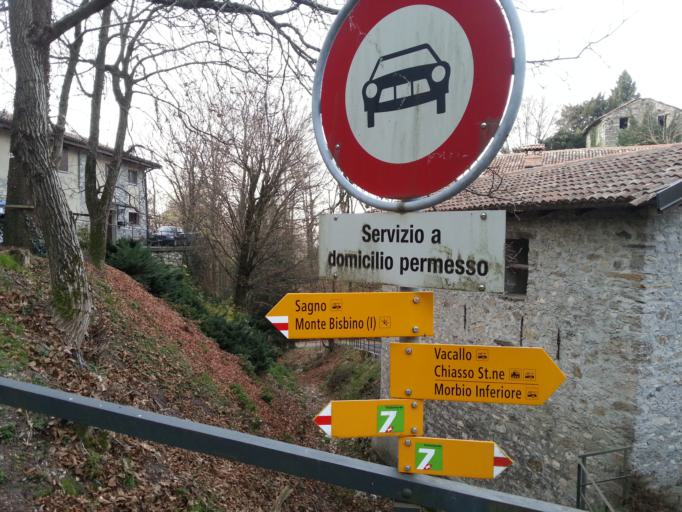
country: IT
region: Lombardy
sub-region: Provincia di Como
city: Maslianico
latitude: 45.8563
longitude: 9.0401
